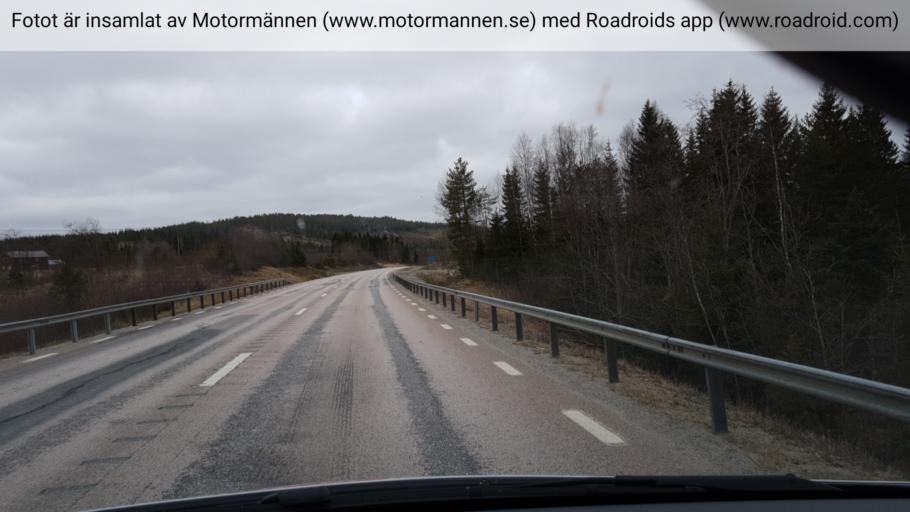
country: SE
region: Vaesternorrland
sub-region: OErnskoeldsviks Kommun
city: Ornskoldsvik
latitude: 63.4165
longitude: 18.5991
